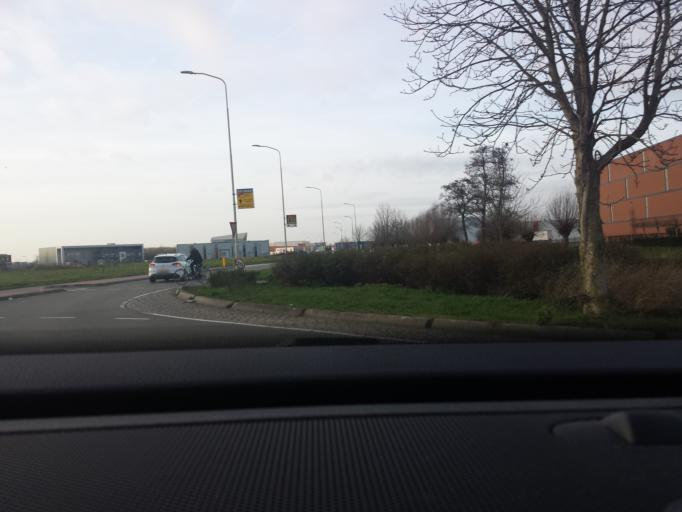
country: NL
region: Gelderland
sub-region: Gemeente Duiven
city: Duiven
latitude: 51.9609
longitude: 6.0128
